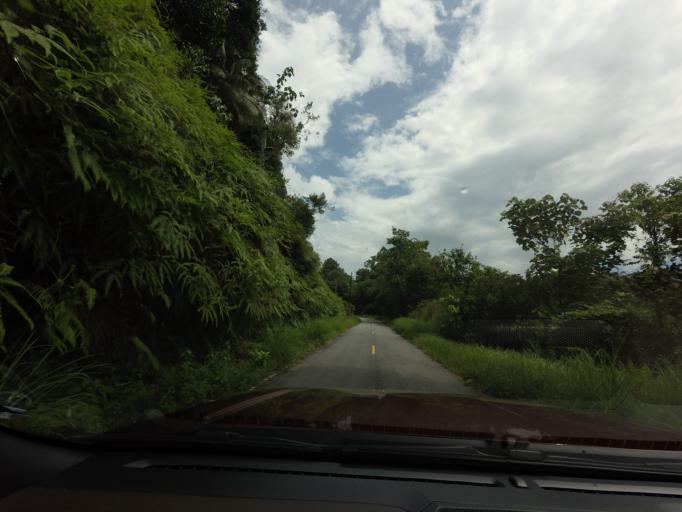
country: TH
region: Narathiwat
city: Sukhirin
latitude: 5.9382
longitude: 101.6512
